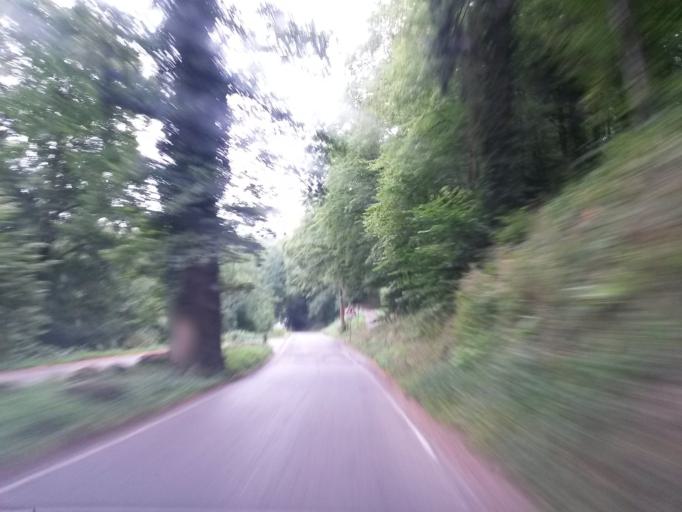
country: DE
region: Baden-Wuerttemberg
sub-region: Karlsruhe Region
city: Pforzheim
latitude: 48.8695
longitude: 8.6779
